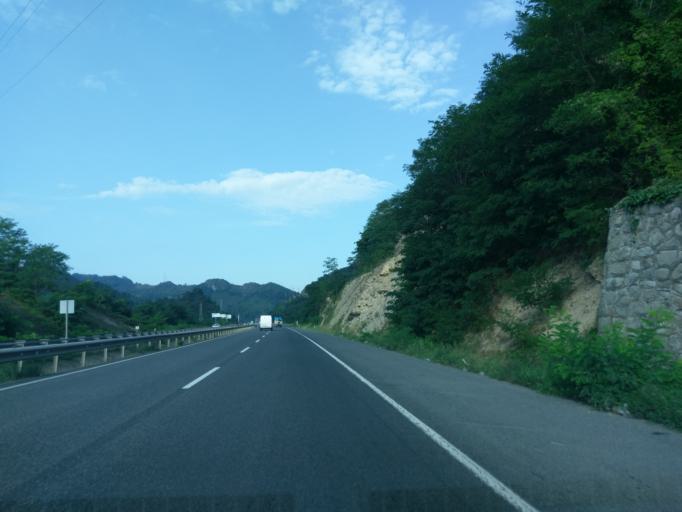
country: TR
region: Ordu
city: Ordu
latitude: 40.9887
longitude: 37.8023
